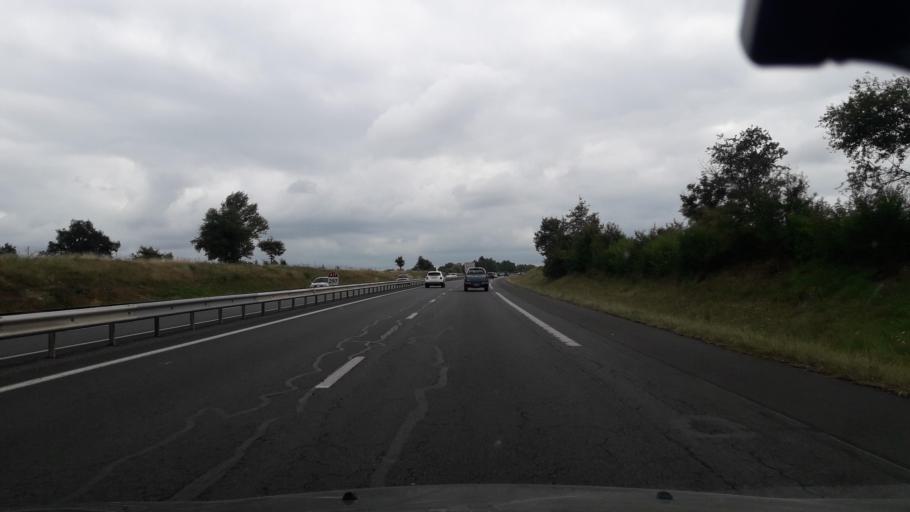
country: FR
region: Auvergne
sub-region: Departement de l'Allier
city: Doyet
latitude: 46.3824
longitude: 2.7276
